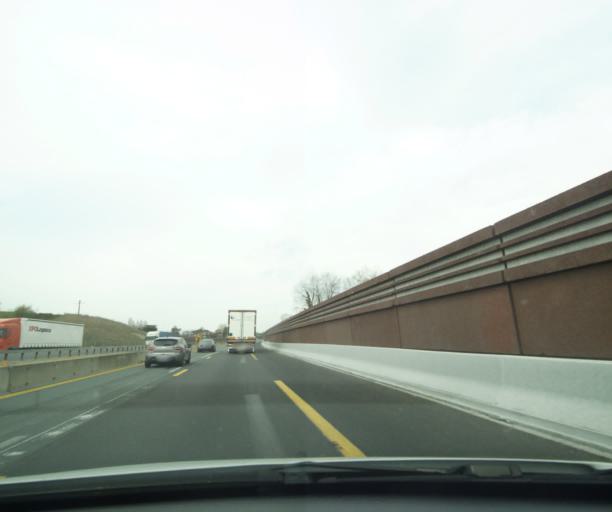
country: FR
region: Aquitaine
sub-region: Departement des Pyrenees-Atlantiques
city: Saint-Jean-de-Luz
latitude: 43.3838
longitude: -1.6435
